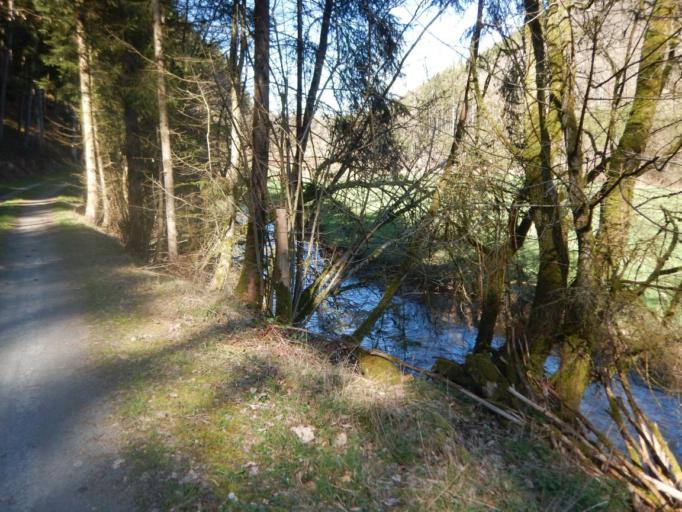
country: LU
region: Diekirch
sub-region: Canton de Wiltz
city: Eschweiler
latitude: 49.9763
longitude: 5.9688
